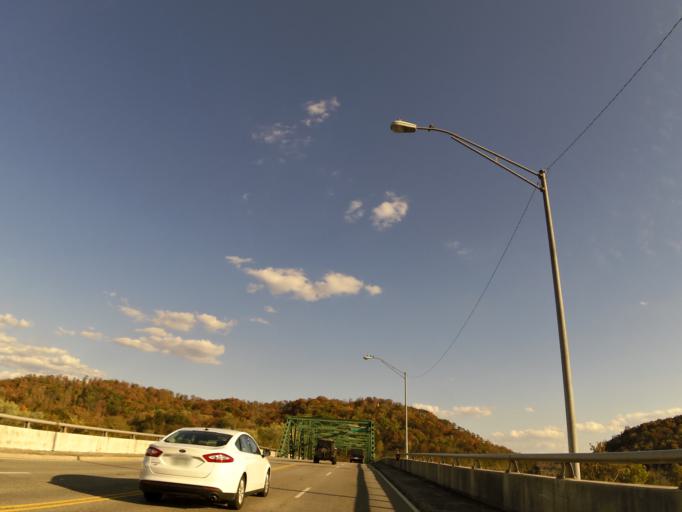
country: US
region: Tennessee
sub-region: Anderson County
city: Clinton
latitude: 36.0948
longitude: -84.1336
